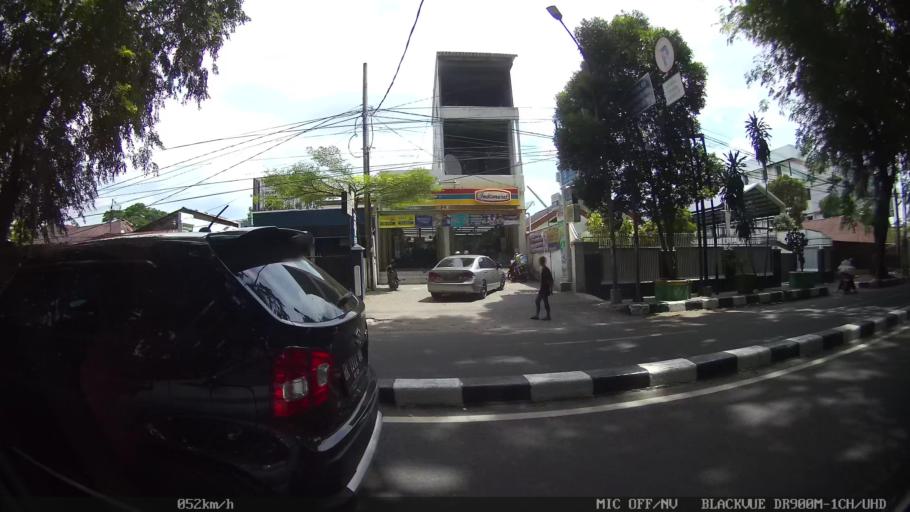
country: ID
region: North Sumatra
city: Medan
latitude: 3.5712
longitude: 98.6682
